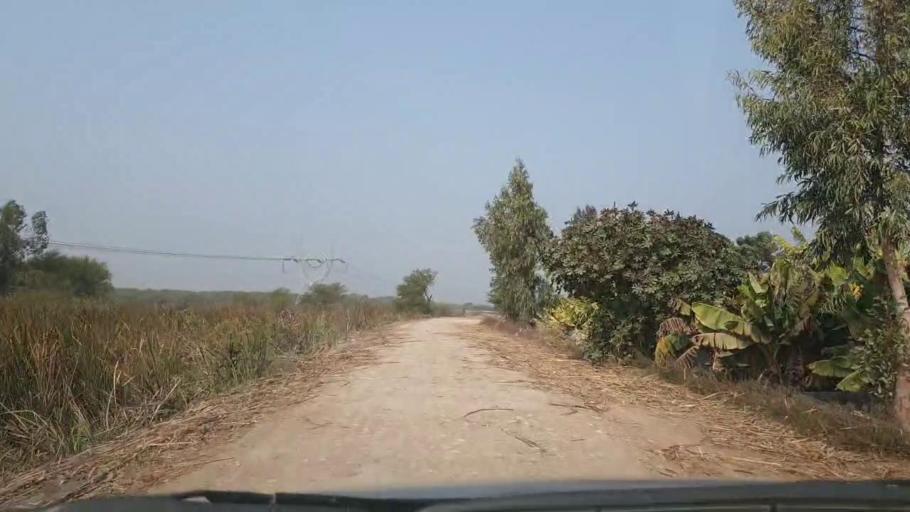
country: PK
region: Sindh
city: Matiari
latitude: 25.6609
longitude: 68.5433
